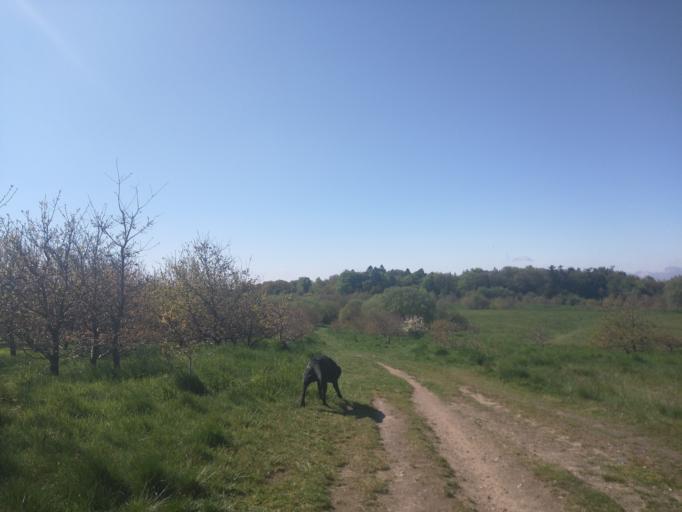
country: DK
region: Central Jutland
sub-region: Viborg Kommune
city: Viborg
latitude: 56.4426
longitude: 9.4322
